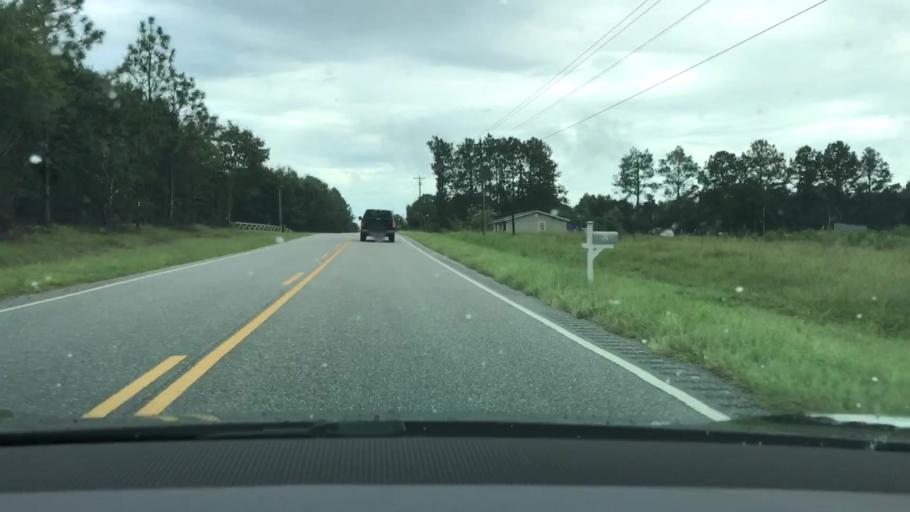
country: US
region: Alabama
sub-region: Geneva County
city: Samson
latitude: 31.0928
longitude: -86.1105
